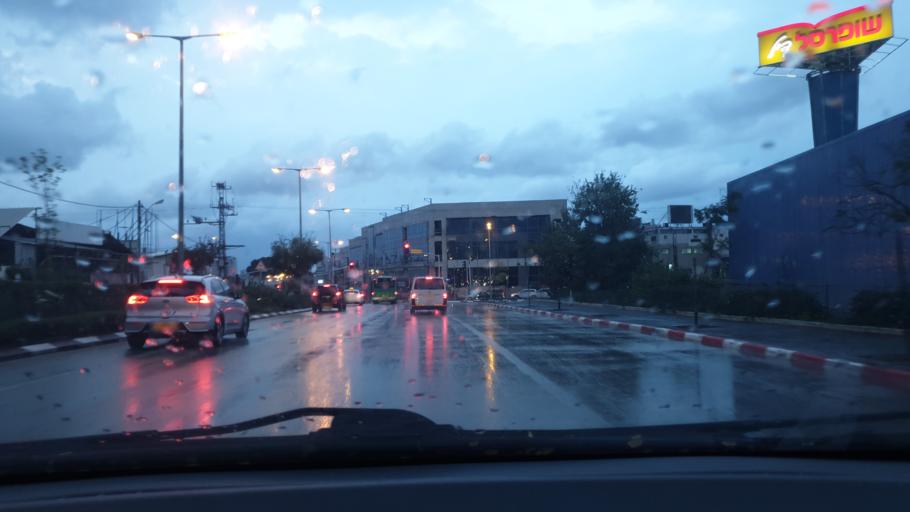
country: IL
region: Central District
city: Rishon LeZiyyon
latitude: 31.9758
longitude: 34.8123
